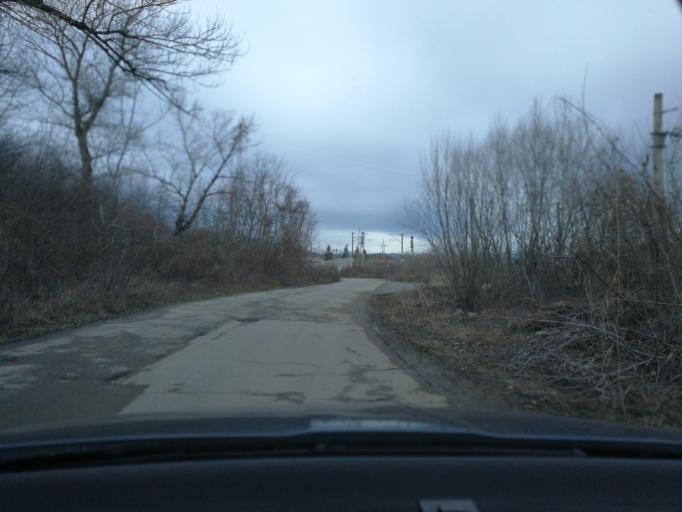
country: RO
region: Prahova
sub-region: Comuna Poiana Campina
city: Poiana Campina
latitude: 45.1400
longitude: 25.6985
